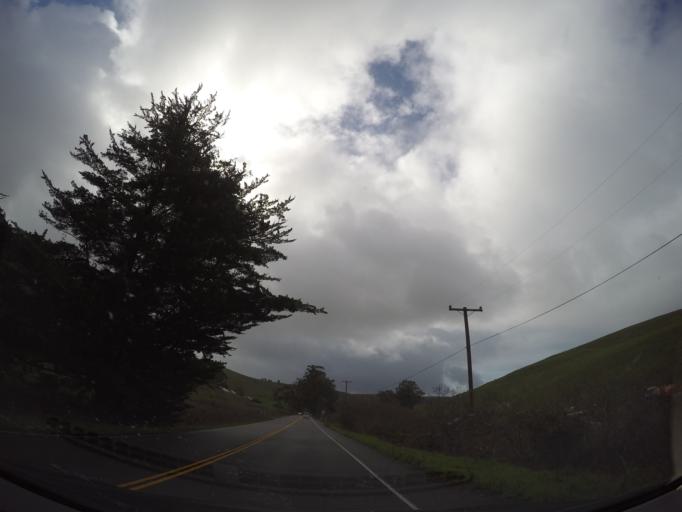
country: US
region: California
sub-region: Sonoma County
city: Bodega Bay
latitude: 38.3342
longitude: -122.9937
